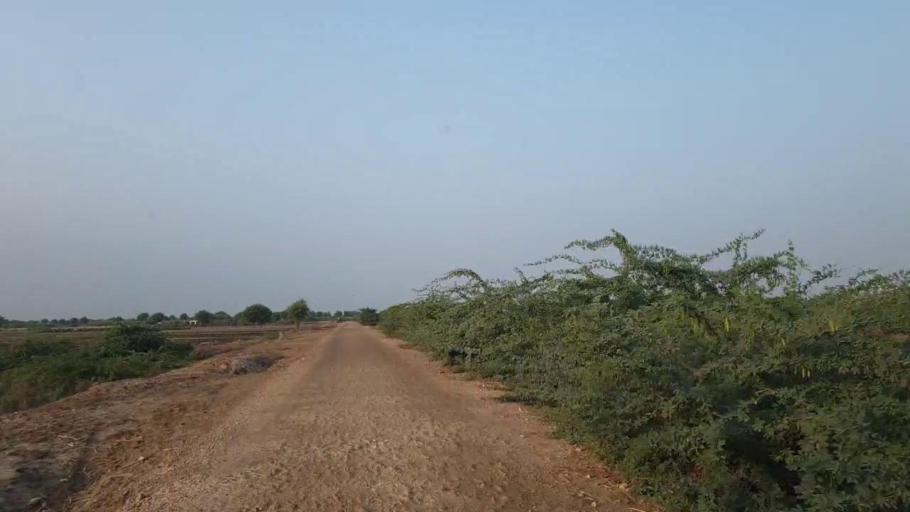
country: PK
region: Sindh
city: Tando Ghulam Ali
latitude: 25.0636
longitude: 68.9605
